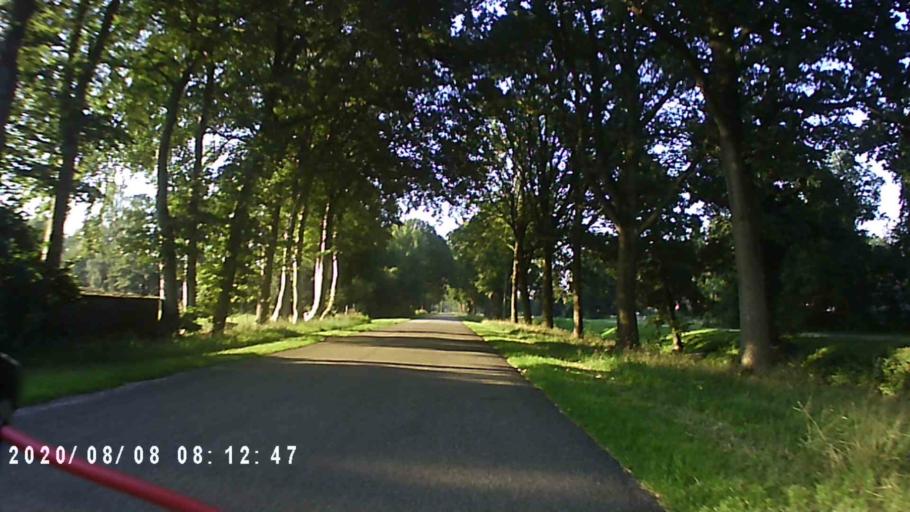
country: NL
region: Groningen
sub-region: Gemeente Leek
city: Leek
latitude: 53.1026
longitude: 6.3396
